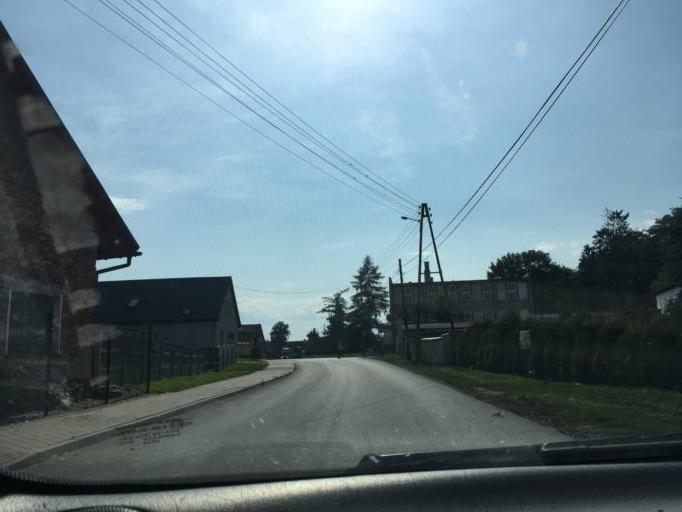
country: PL
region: Opole Voivodeship
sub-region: Powiat prudnicki
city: Raclawice Slaskie
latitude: 50.3030
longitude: 17.8089
